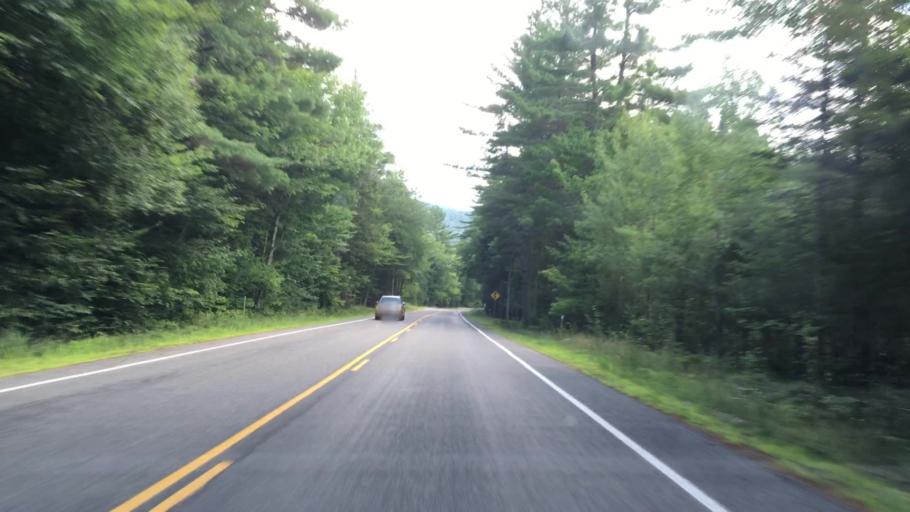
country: US
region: New Hampshire
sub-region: Grafton County
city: Woodstock
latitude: 44.0740
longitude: -71.7947
